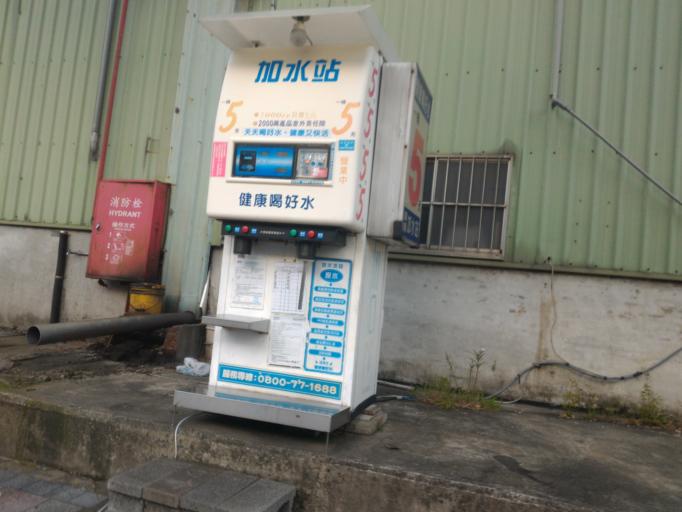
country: TW
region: Taiwan
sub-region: Taoyuan
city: Taoyuan
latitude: 24.9580
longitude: 121.3902
